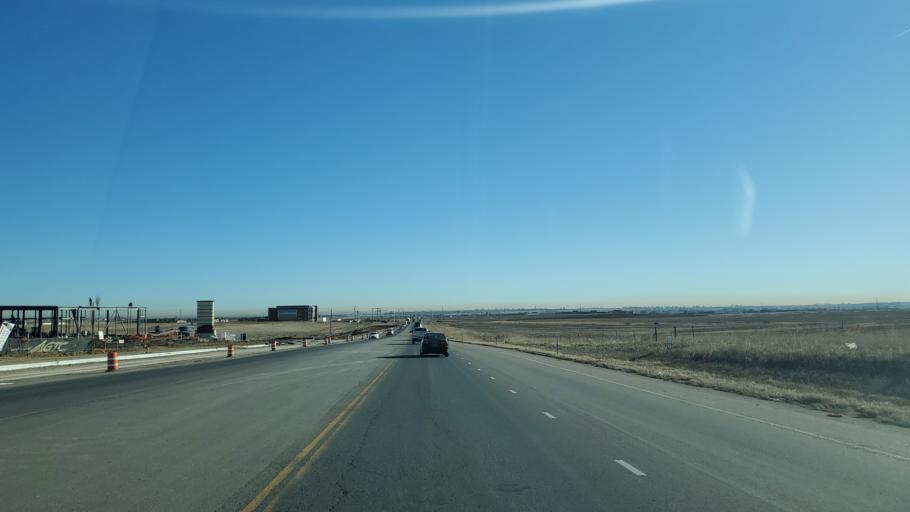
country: US
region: Colorado
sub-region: Boulder County
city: Erie
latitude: 40.0006
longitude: -105.0047
